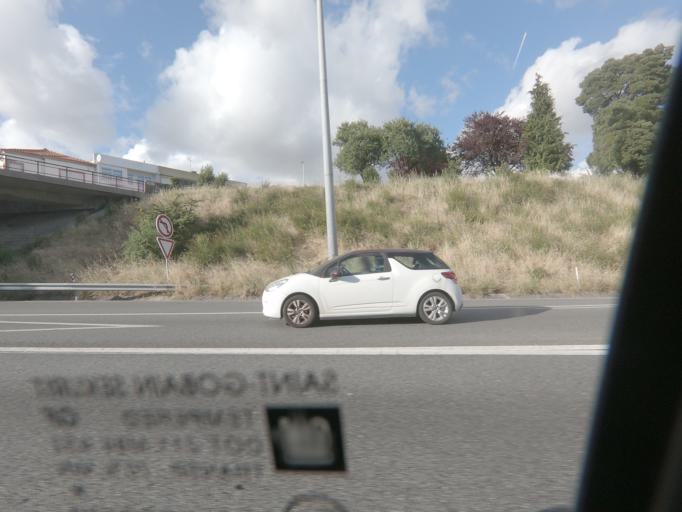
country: PT
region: Porto
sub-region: Porto
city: Porto
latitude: 41.1732
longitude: -8.6073
